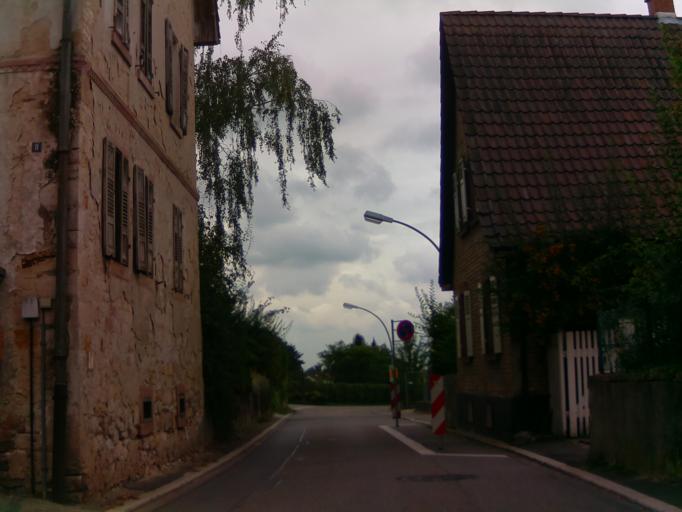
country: DE
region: Baden-Wuerttemberg
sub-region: Karlsruhe Region
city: Weinheim
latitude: 49.5179
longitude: 8.6669
